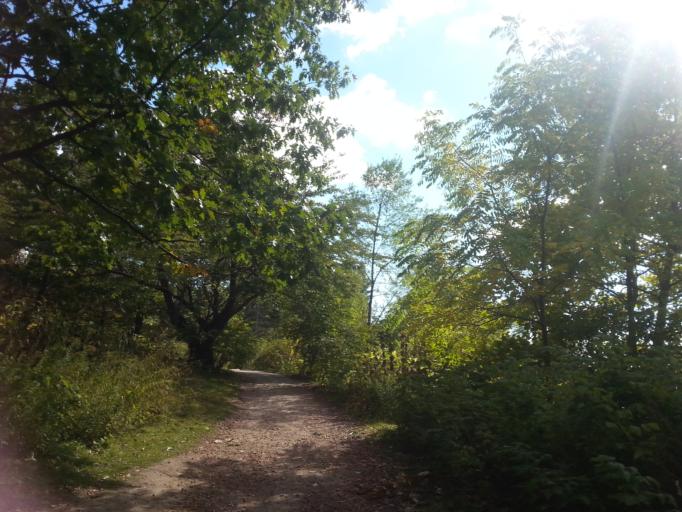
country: CA
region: Ontario
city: Toronto
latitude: 43.6442
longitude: -79.4682
